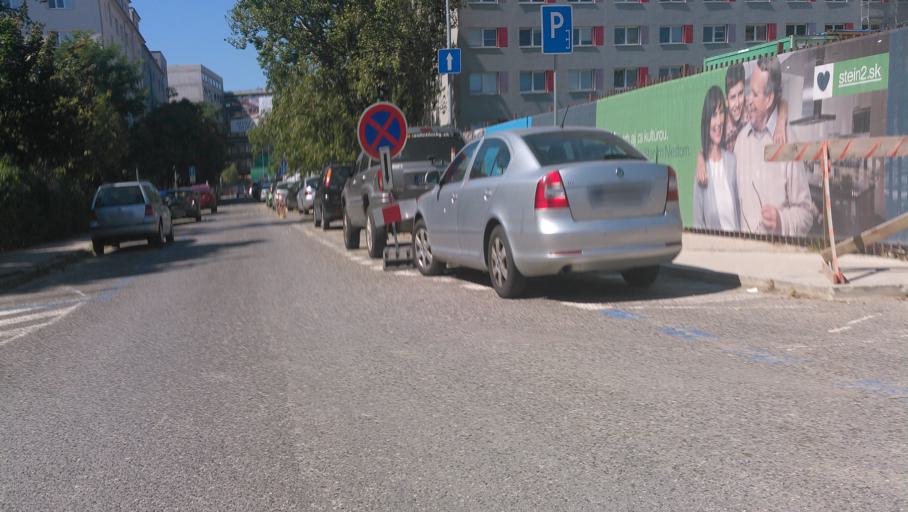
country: SK
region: Bratislavsky
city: Bratislava
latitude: 48.1553
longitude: 17.1218
